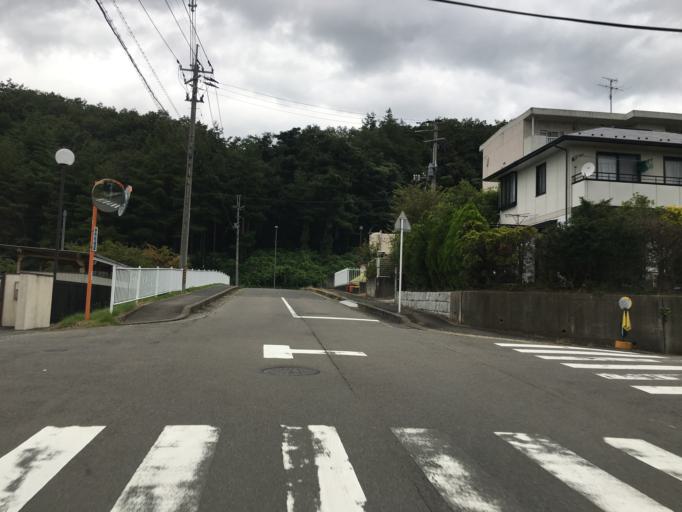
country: JP
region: Fukushima
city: Fukushima-shi
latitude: 37.6931
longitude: 140.4840
